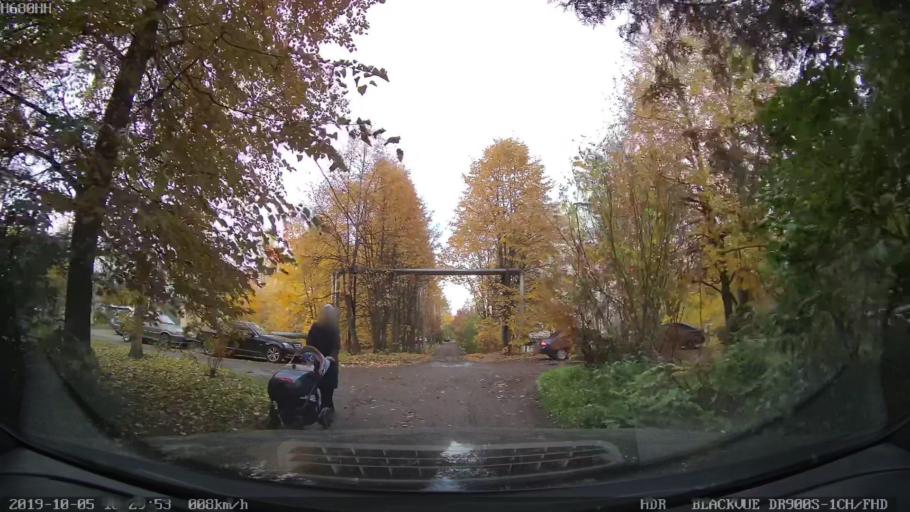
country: RU
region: Moskovskaya
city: Solnechnogorsk
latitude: 56.2176
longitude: 37.0335
